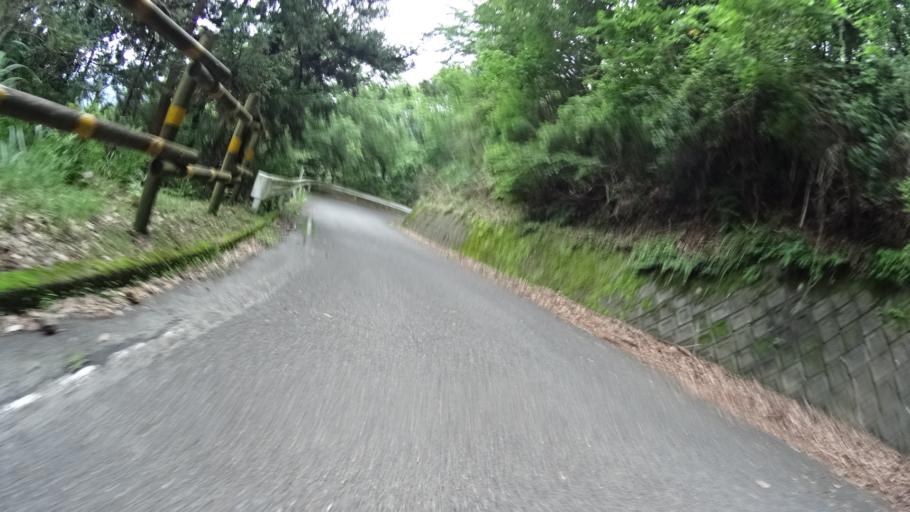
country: JP
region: Kanagawa
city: Atsugi
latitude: 35.5000
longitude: 139.2693
